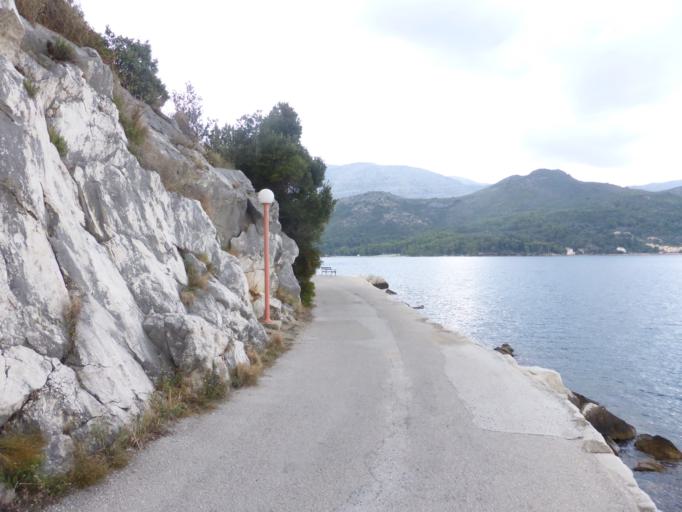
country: HR
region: Dubrovacko-Neretvanska
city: Podgora
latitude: 42.7800
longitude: 17.8736
